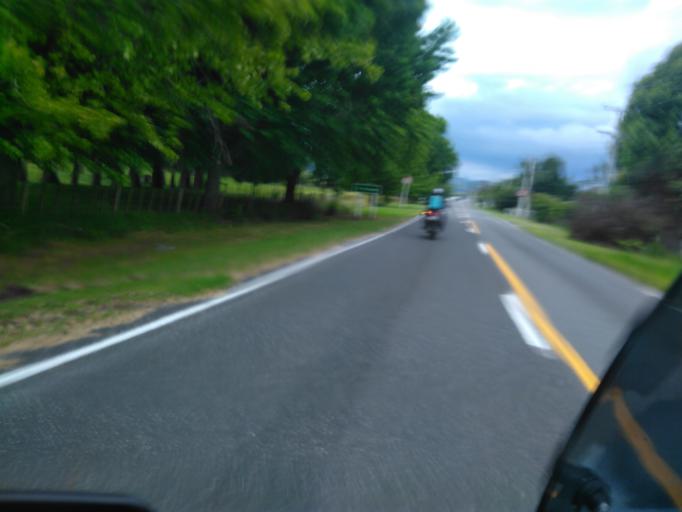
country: NZ
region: Gisborne
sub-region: Gisborne District
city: Gisborne
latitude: -38.4741
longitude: 177.8624
